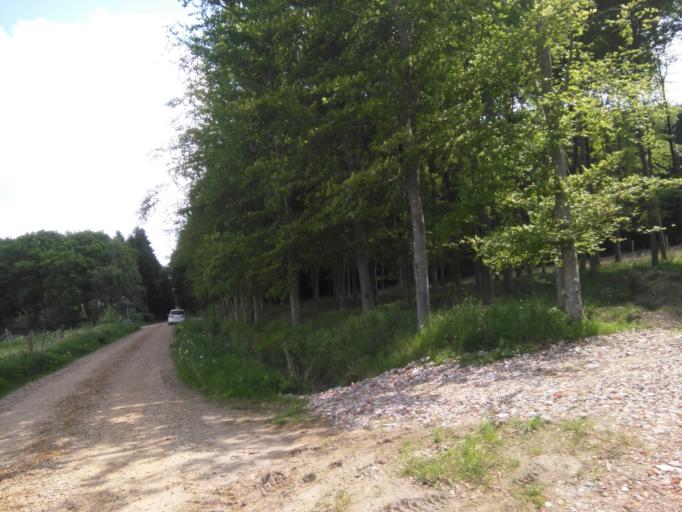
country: DK
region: Central Jutland
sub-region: Favrskov Kommune
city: Hammel
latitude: 56.2733
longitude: 9.9494
